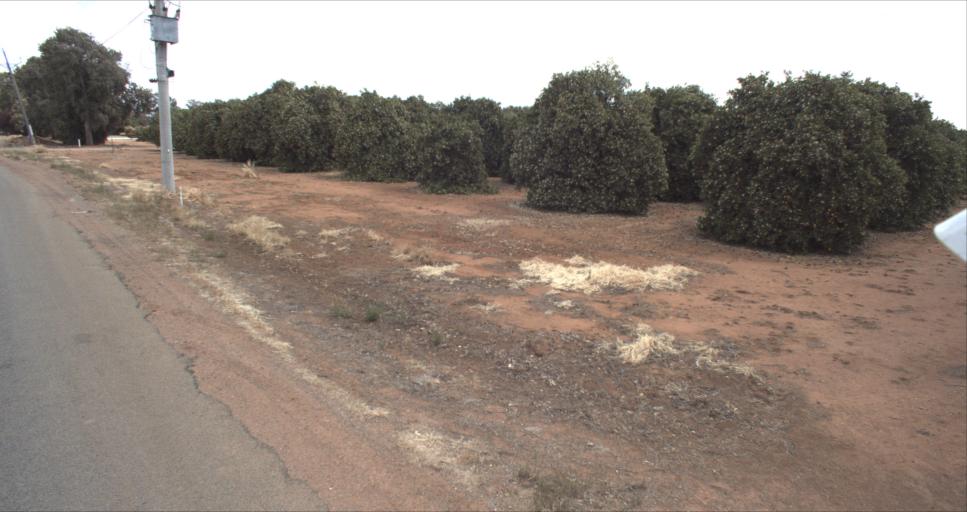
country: AU
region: New South Wales
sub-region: Leeton
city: Leeton
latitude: -34.5810
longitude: 146.3969
